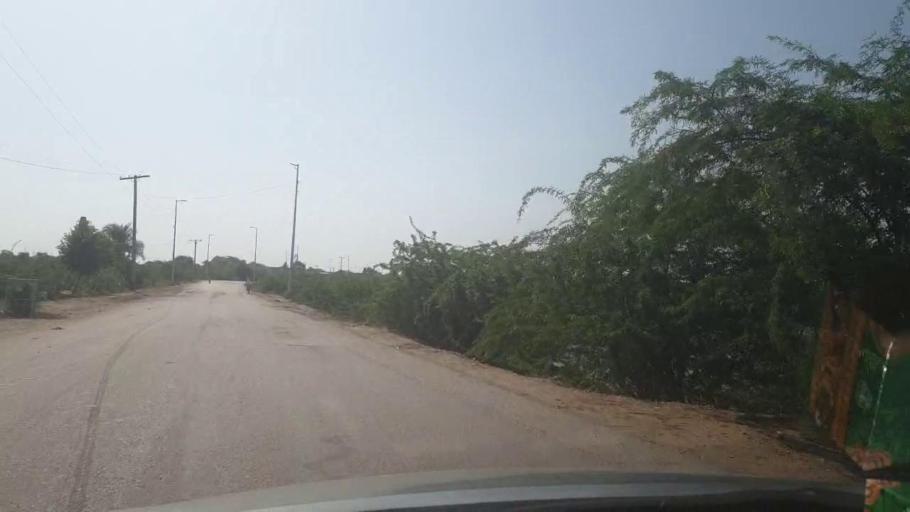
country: PK
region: Sindh
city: Rohri
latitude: 27.5048
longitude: 69.0374
